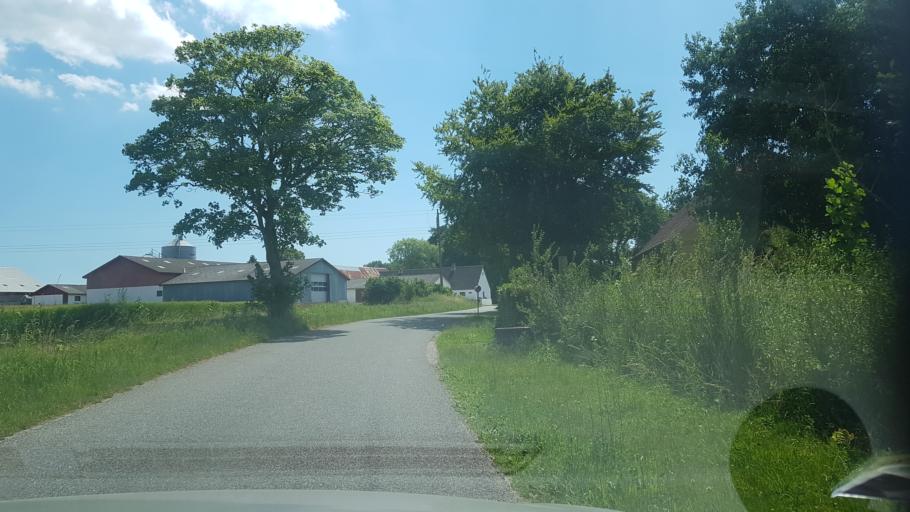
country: DK
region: Zealand
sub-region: Kalundborg Kommune
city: Svebolle
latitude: 55.7017
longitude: 11.2923
